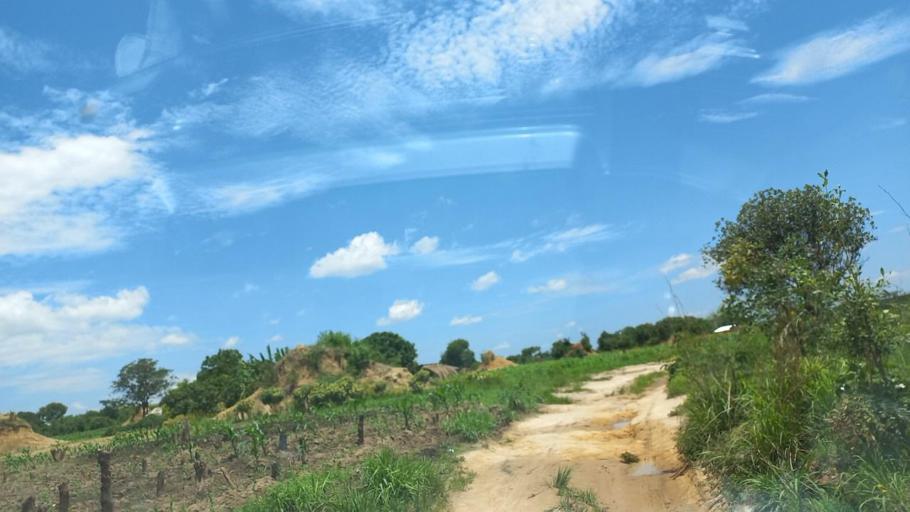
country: ZM
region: Copperbelt
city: Ndola
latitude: -12.8791
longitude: 28.4476
